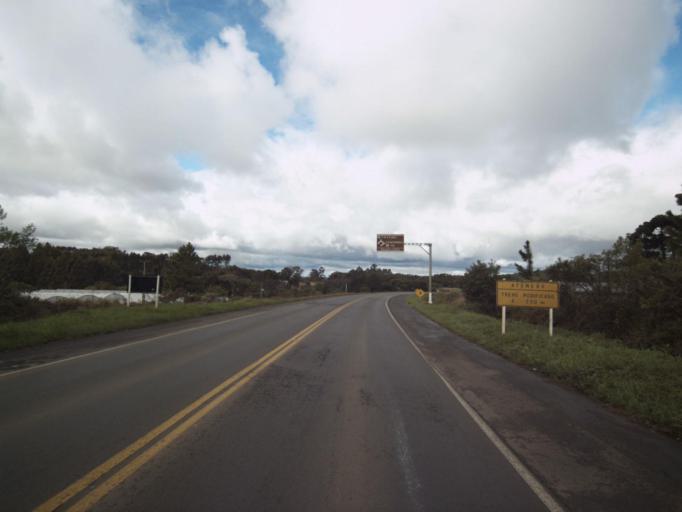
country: BR
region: Santa Catarina
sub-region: Concordia
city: Concordia
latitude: -27.2208
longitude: -51.9488
